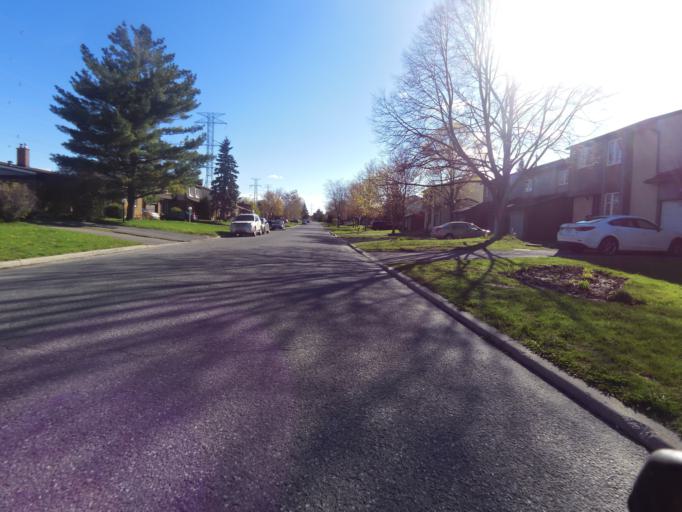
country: CA
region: Ontario
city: Ottawa
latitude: 45.3323
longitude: -75.7413
